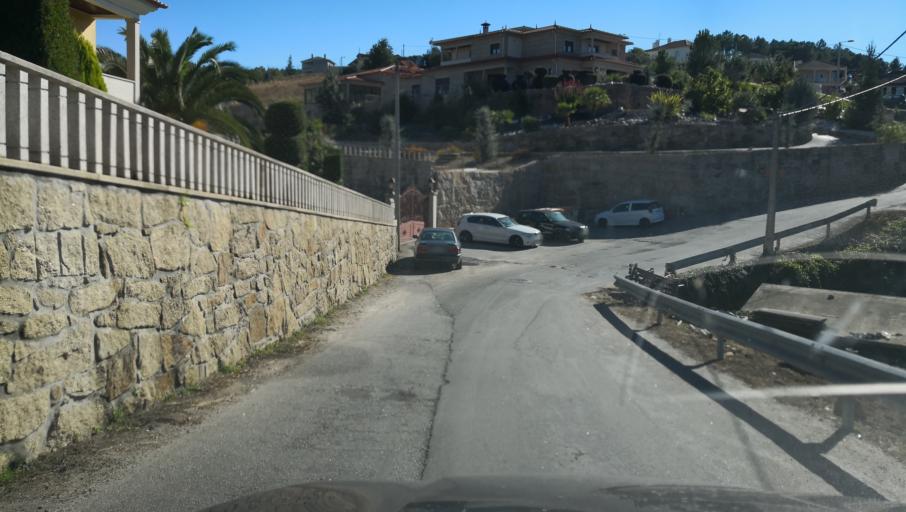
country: PT
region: Vila Real
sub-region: Vila Real
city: Vila Real
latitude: 41.2876
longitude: -7.7174
